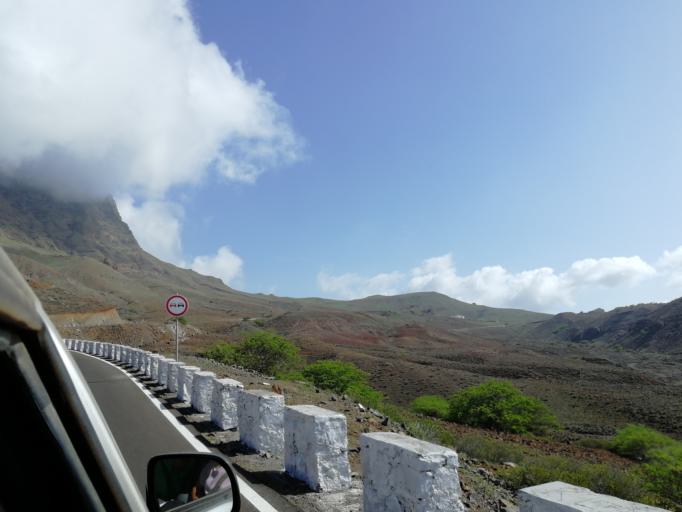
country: CV
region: Sao Vicente
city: Mindelo
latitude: 16.8848
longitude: -24.9410
